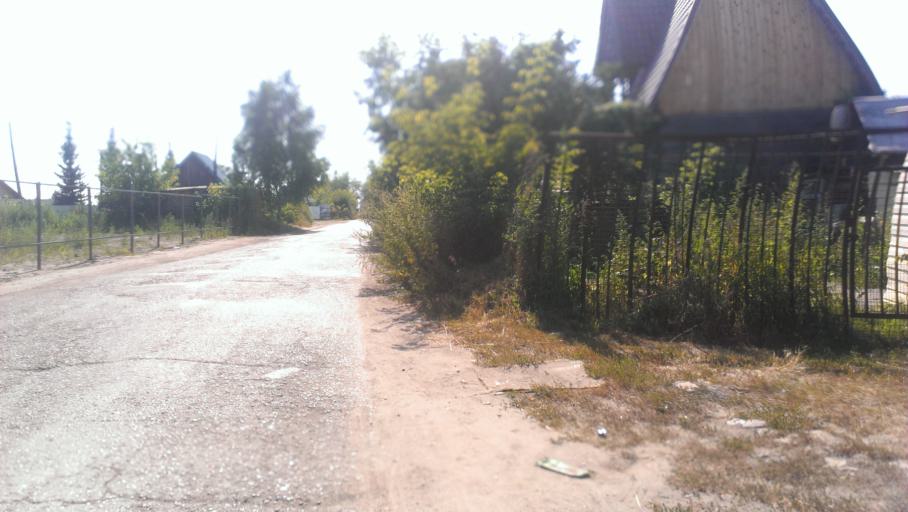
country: RU
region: Altai Krai
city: Novosilikatnyy
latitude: 53.3232
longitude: 83.6836
